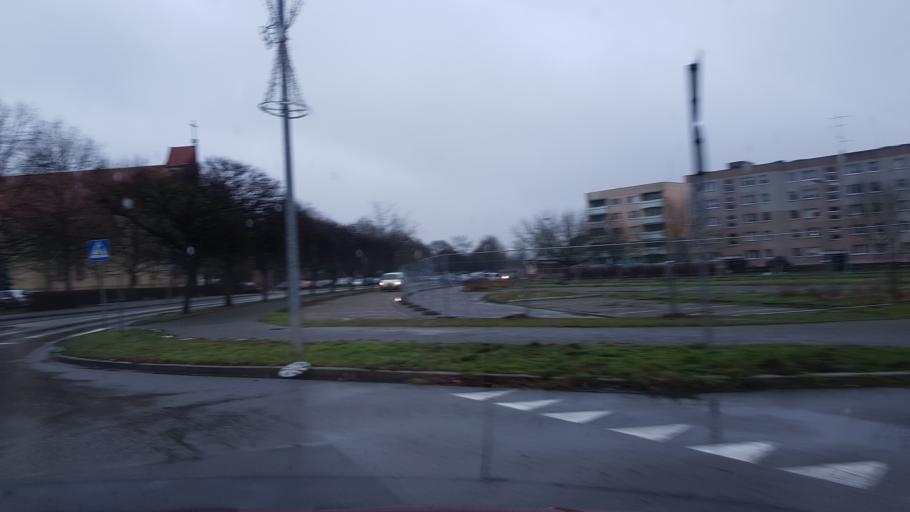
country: PL
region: West Pomeranian Voivodeship
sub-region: Powiat policki
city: Police
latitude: 53.5405
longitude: 14.5471
